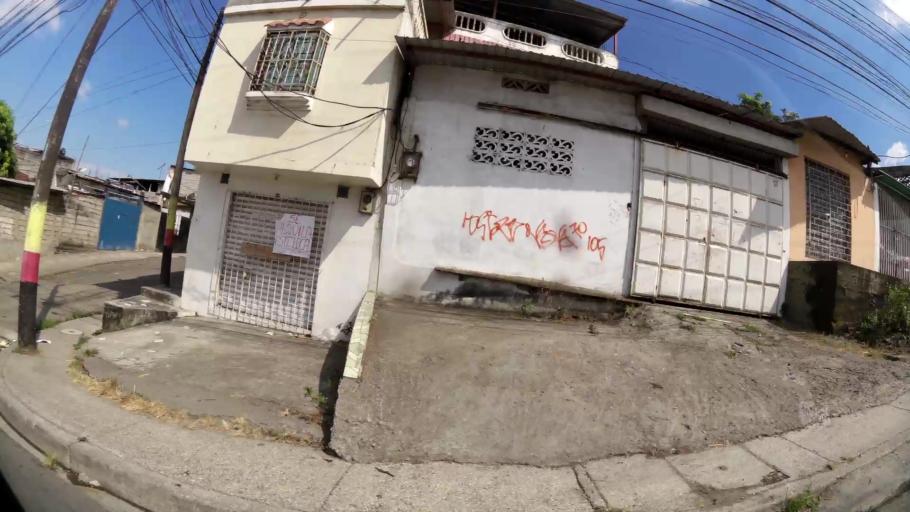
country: EC
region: Guayas
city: Santa Lucia
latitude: -2.1398
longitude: -79.9427
